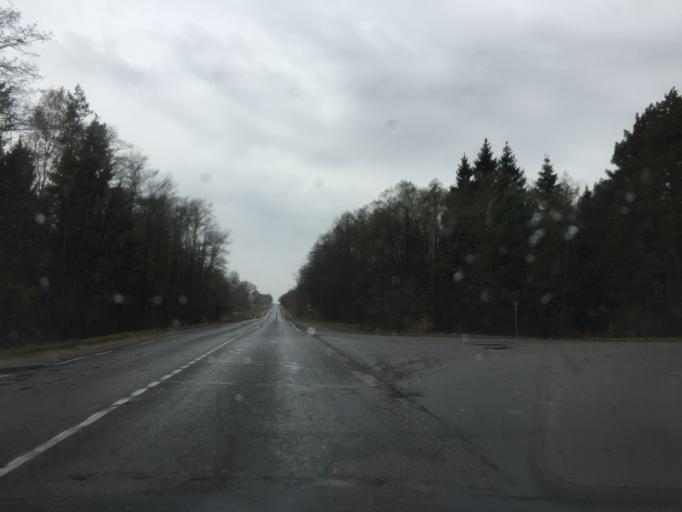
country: BY
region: Mogilev
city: Slawharad
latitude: 53.4072
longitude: 30.9352
